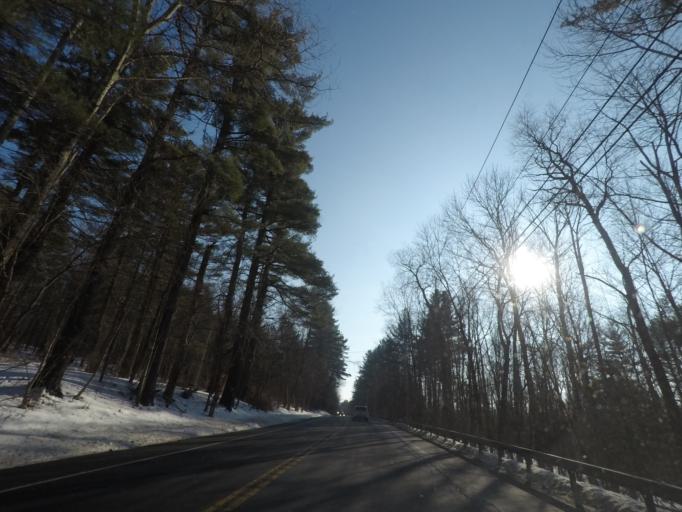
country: US
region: Massachusetts
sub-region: Berkshire County
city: Richmond
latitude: 42.4953
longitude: -73.3715
